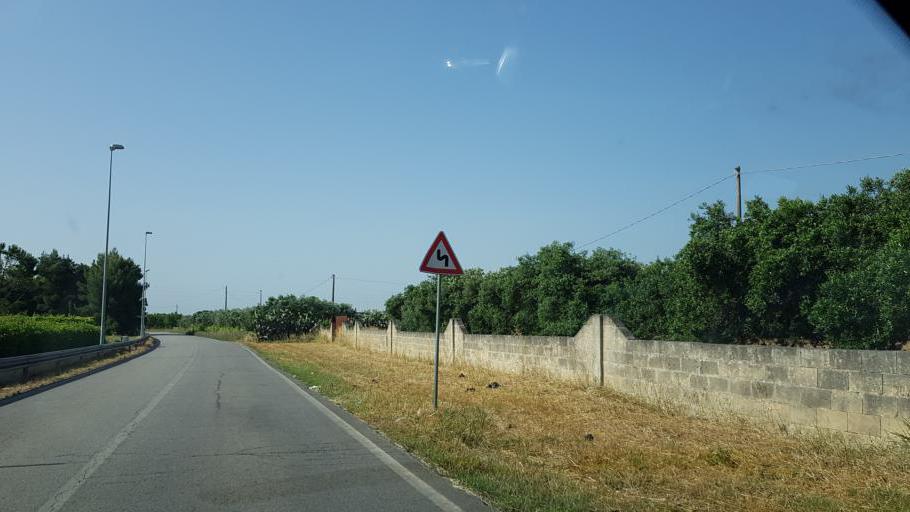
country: IT
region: Apulia
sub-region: Provincia di Brindisi
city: Mesagne
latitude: 40.5406
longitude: 17.8168
